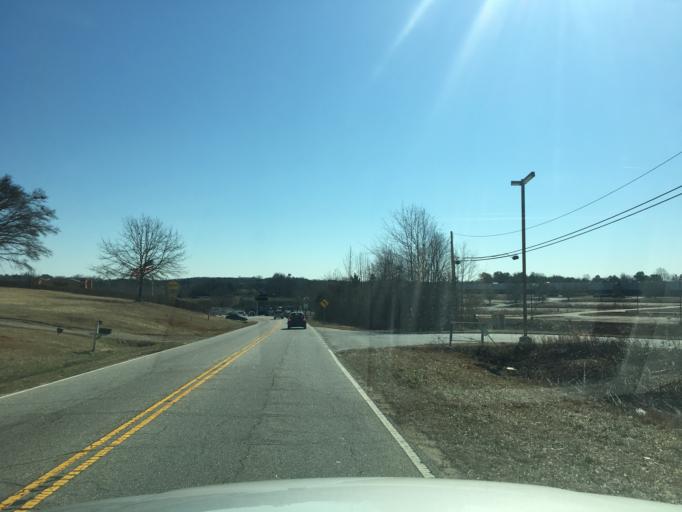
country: US
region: South Carolina
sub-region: Pickens County
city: Liberty
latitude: 34.7778
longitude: -82.6744
